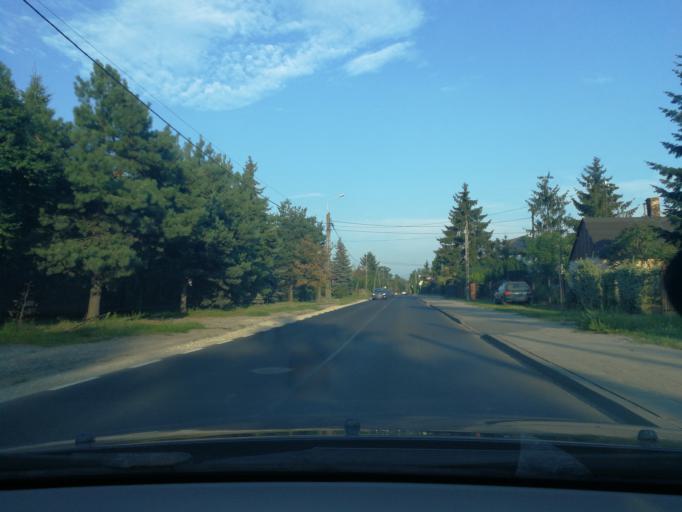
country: PL
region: Masovian Voivodeship
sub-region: Powiat warszawski zachodni
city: Ozarow Mazowiecki
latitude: 52.1892
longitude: 20.7578
